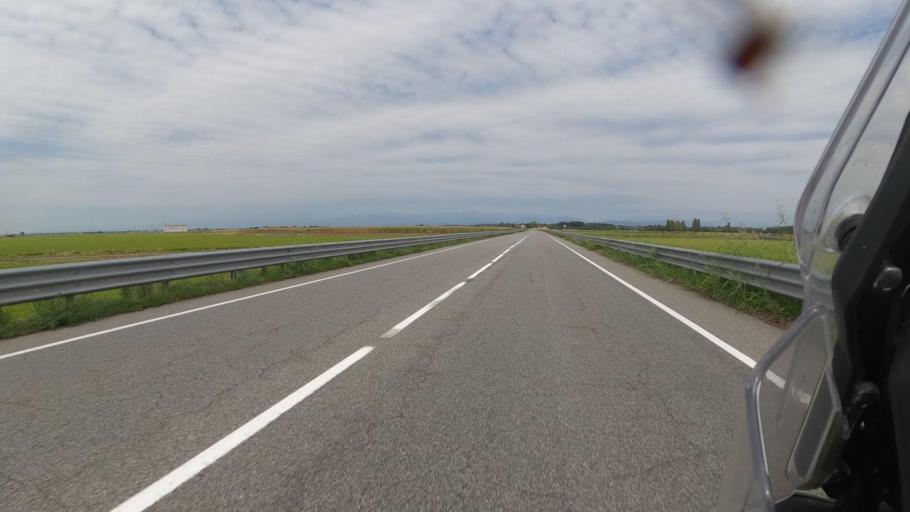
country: IT
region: Piedmont
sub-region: Provincia di Novara
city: Caltignaga
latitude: 45.5138
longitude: 8.5386
